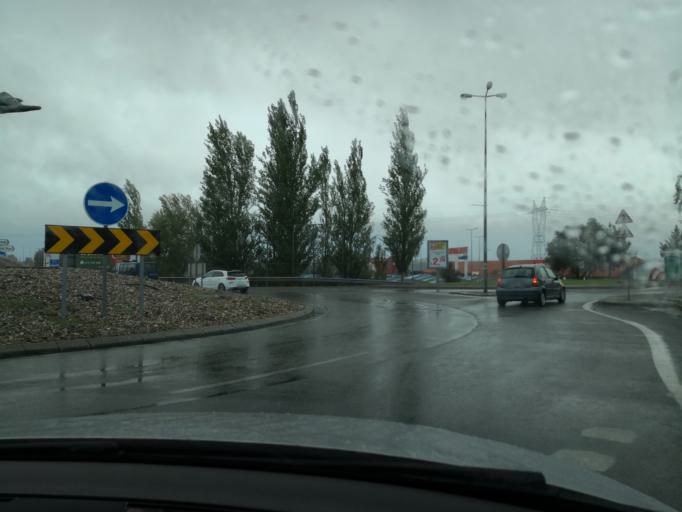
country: PT
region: Setubal
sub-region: Moita
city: Moita
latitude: 38.6451
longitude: -8.9792
